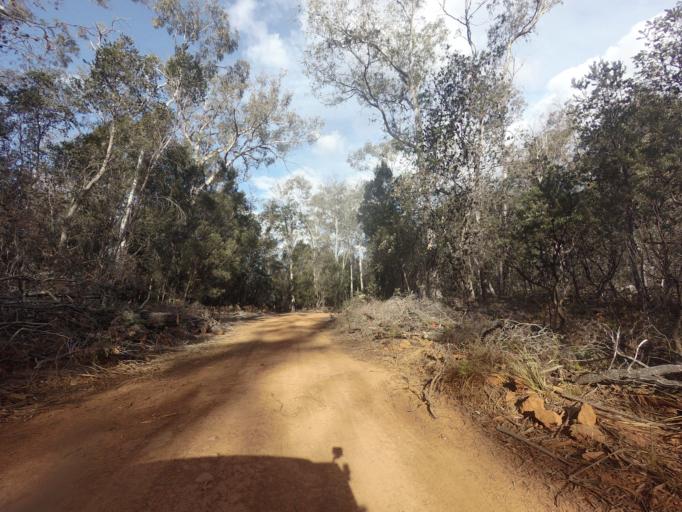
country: AU
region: Tasmania
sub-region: Break O'Day
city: St Helens
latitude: -41.8457
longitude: 148.0940
